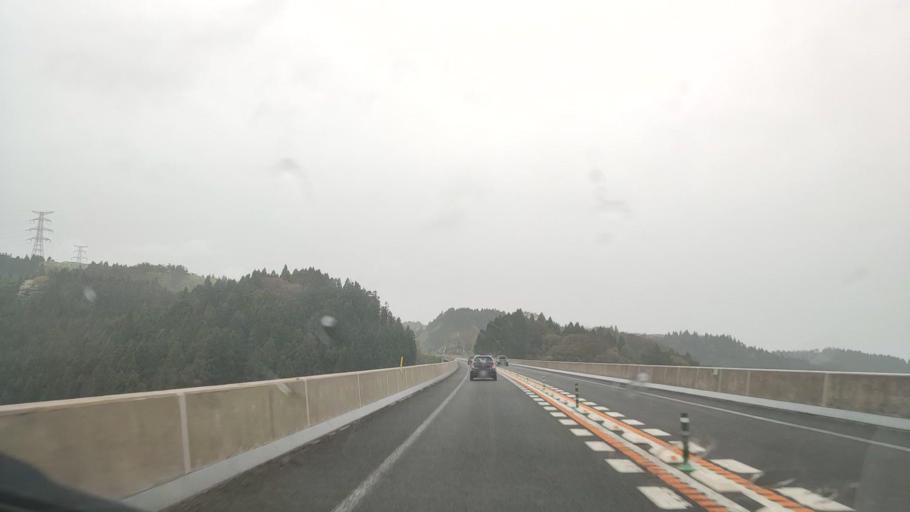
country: JP
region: Akita
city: Noshiromachi
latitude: 40.2001
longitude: 140.1336
